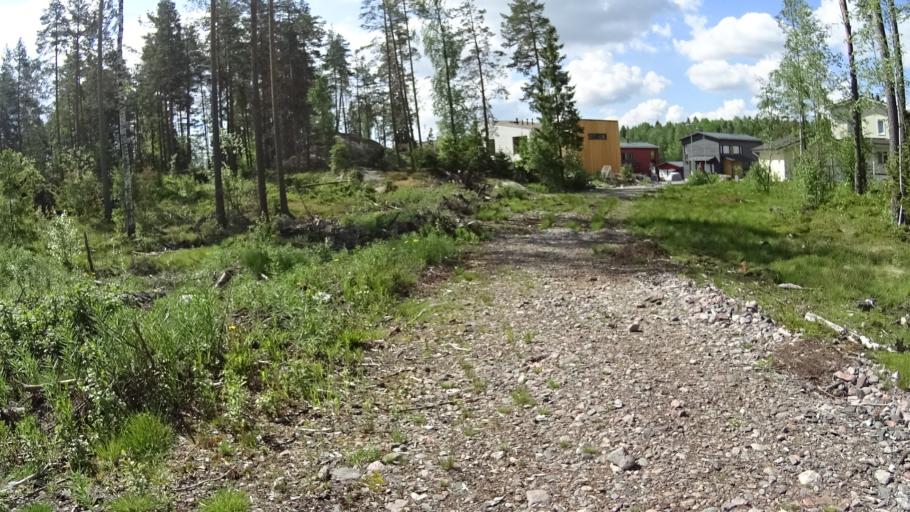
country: FI
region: Uusimaa
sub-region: Helsinki
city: Espoo
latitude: 60.2305
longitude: 24.6386
